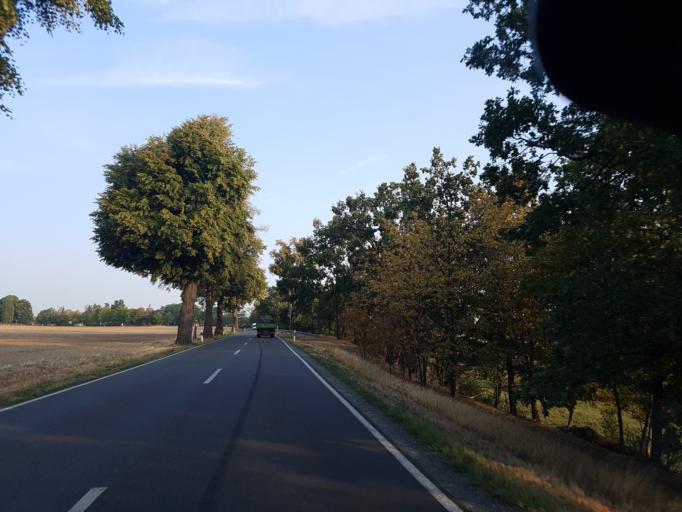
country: DE
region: Saxony
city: Dommitzsch
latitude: 51.6345
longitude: 12.8932
